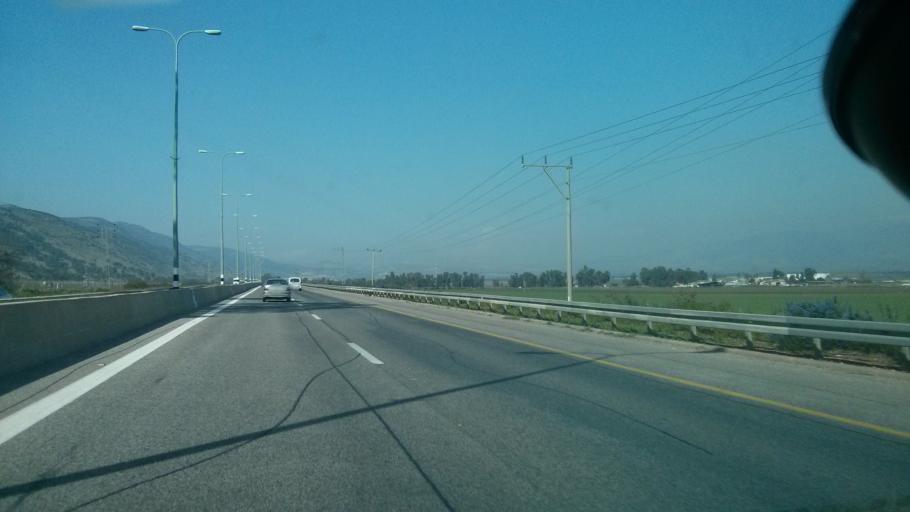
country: IL
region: Northern District
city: Qiryat Shemona
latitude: 33.0995
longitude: 35.5744
